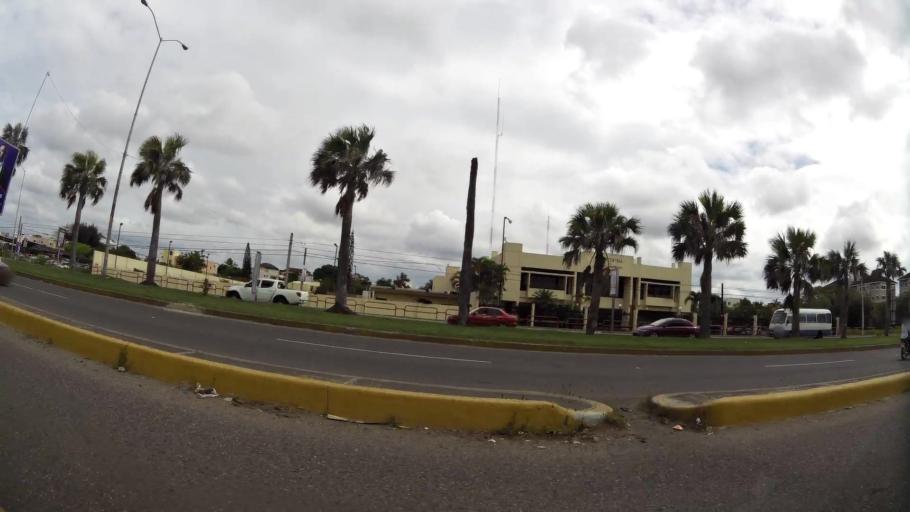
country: DO
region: Santiago
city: Santiago de los Caballeros
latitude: 19.4466
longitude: -70.6742
